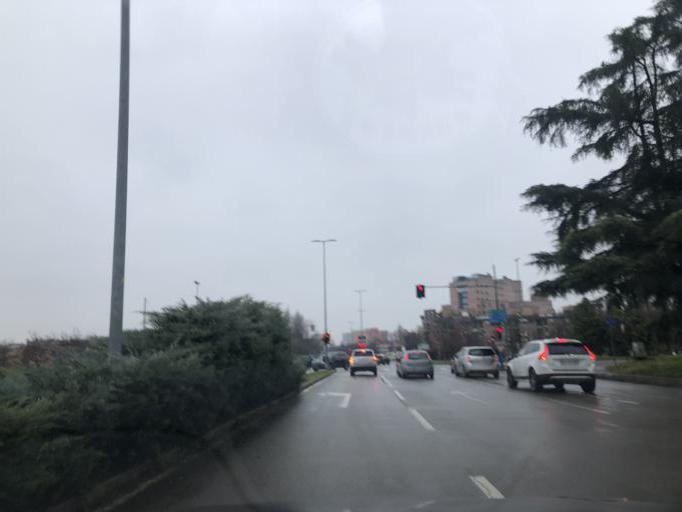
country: IT
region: Emilia-Romagna
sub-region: Provincia di Modena
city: Modena
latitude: 44.6412
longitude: 10.9029
